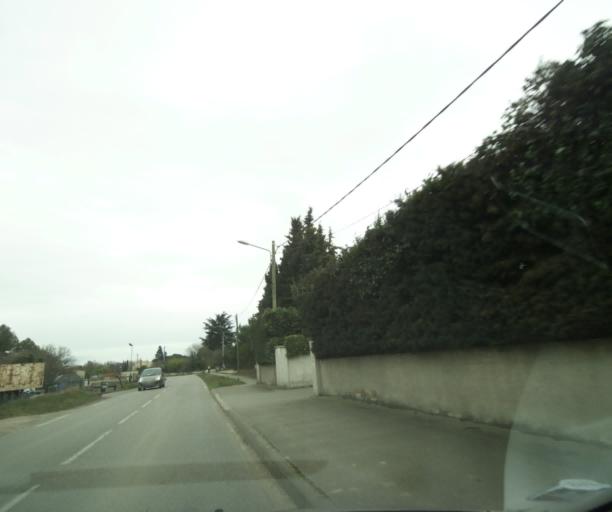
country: FR
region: Provence-Alpes-Cote d'Azur
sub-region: Departement des Bouches-du-Rhone
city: Eguilles
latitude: 43.5761
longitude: 5.4132
